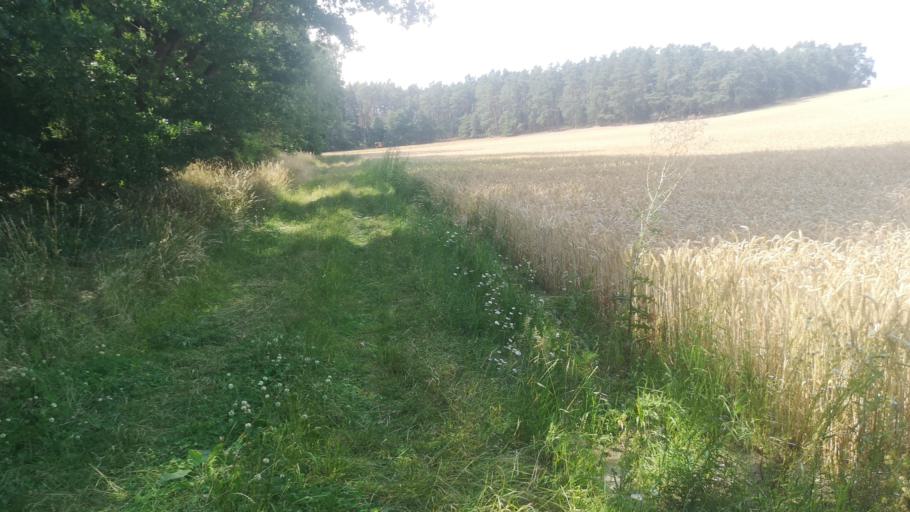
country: DE
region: Lower Saxony
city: Dahlem
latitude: 53.2195
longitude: 10.7480
